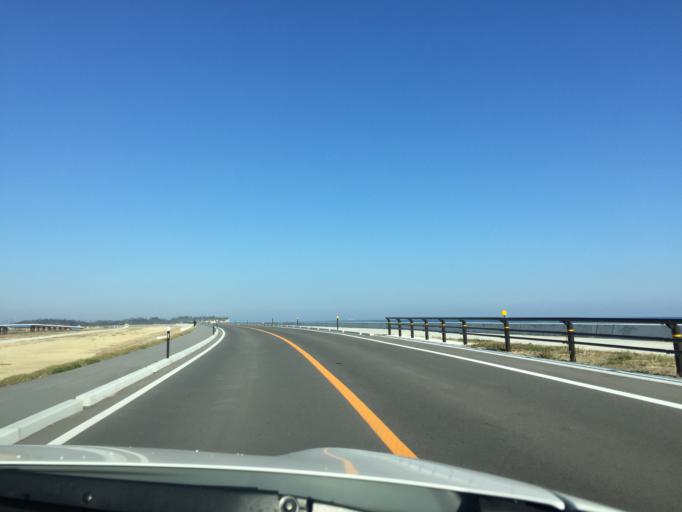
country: JP
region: Miyagi
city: Marumori
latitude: 37.7982
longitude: 140.9858
